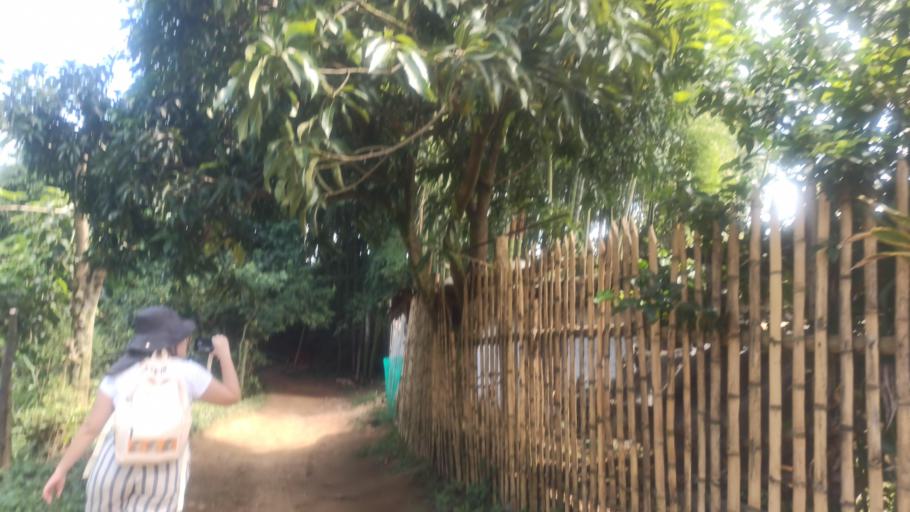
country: CO
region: Valle del Cauca
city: Jamundi
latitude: 3.1885
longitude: -76.6299
